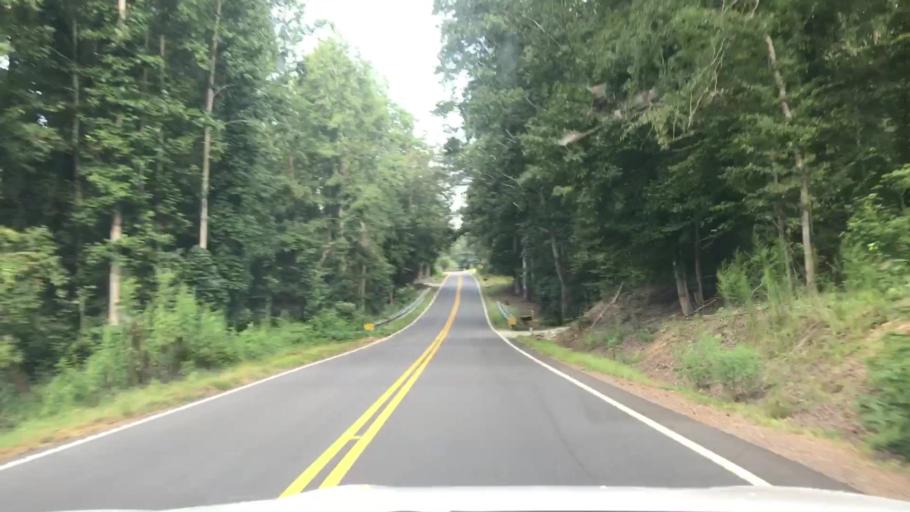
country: US
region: South Carolina
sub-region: Spartanburg County
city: Roebuck
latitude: 34.8252
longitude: -81.9442
